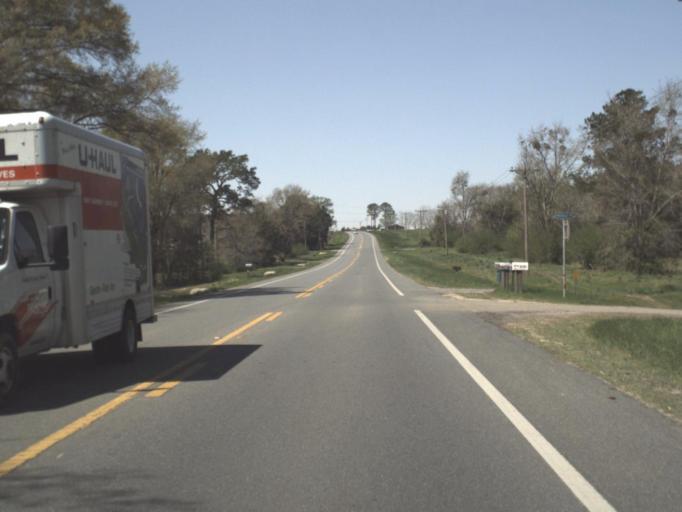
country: US
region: Florida
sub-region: Jackson County
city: Graceville
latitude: 30.9637
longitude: -85.5446
